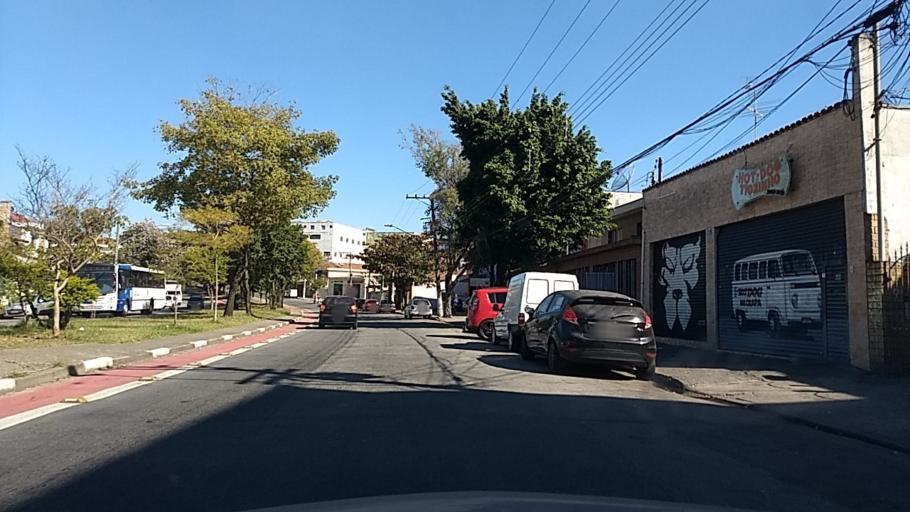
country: BR
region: Sao Paulo
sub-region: Guarulhos
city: Guarulhos
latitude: -23.4964
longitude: -46.5725
